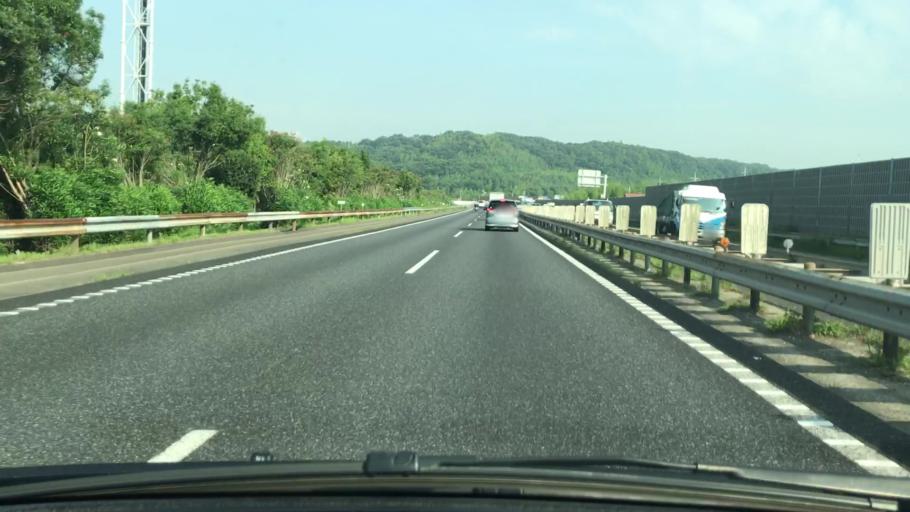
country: JP
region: Hyogo
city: Akashi
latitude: 34.6873
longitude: 134.9753
